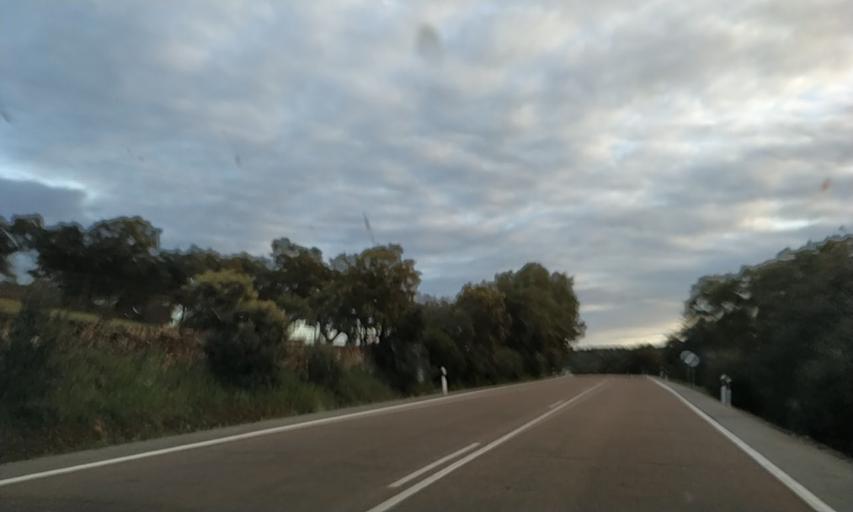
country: ES
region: Extremadura
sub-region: Provincia de Badajoz
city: Puebla de Obando
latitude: 39.2544
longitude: -6.5550
